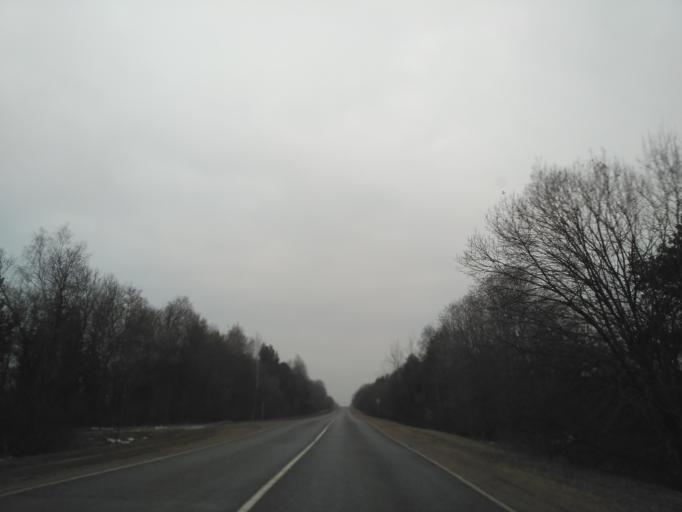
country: BY
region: Minsk
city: Haradzyeya
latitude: 53.3201
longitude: 26.4361
